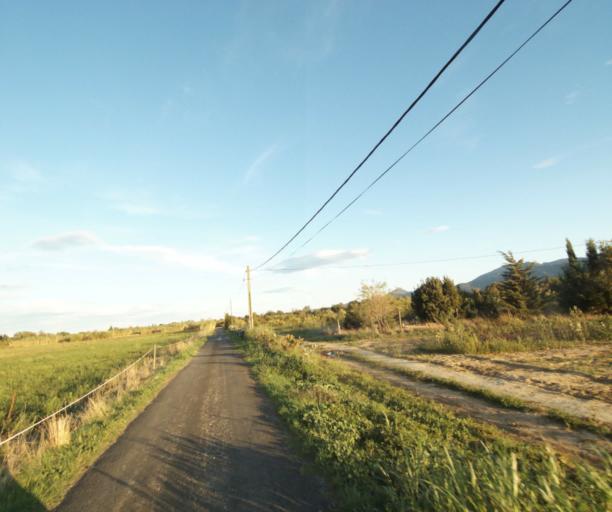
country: FR
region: Languedoc-Roussillon
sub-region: Departement des Pyrenees-Orientales
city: Latour-Bas-Elne
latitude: 42.5822
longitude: 2.9954
